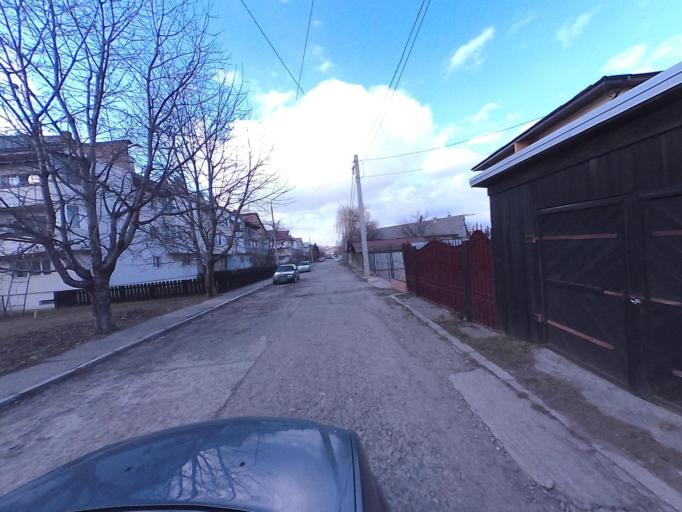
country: RO
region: Neamt
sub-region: Oras Targu Neamt
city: Targu Neamt
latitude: 47.2032
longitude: 26.3758
